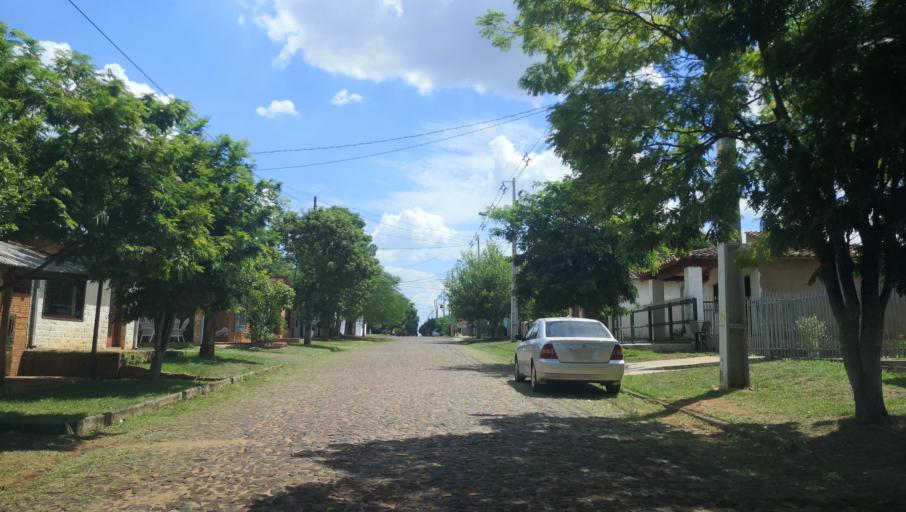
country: PY
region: Misiones
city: Santa Maria
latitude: -26.8920
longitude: -57.0183
